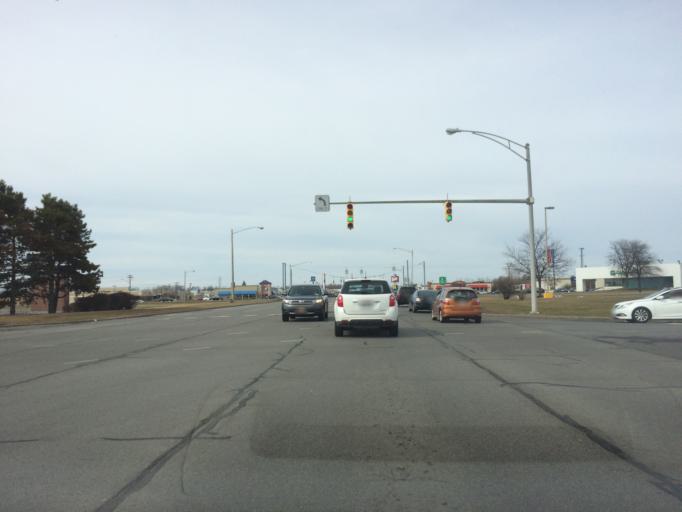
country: US
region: New York
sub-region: Monroe County
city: Rochester
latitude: 43.0852
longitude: -77.6297
